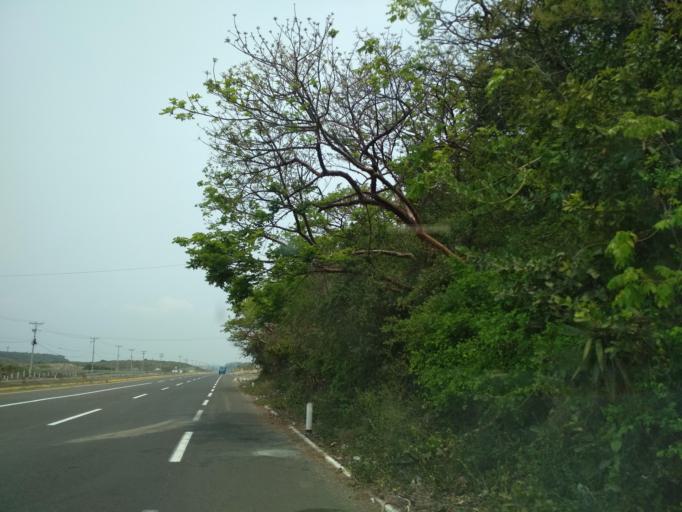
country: MX
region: Veracruz
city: Anton Lizardo
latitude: 19.0532
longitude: -96.0282
